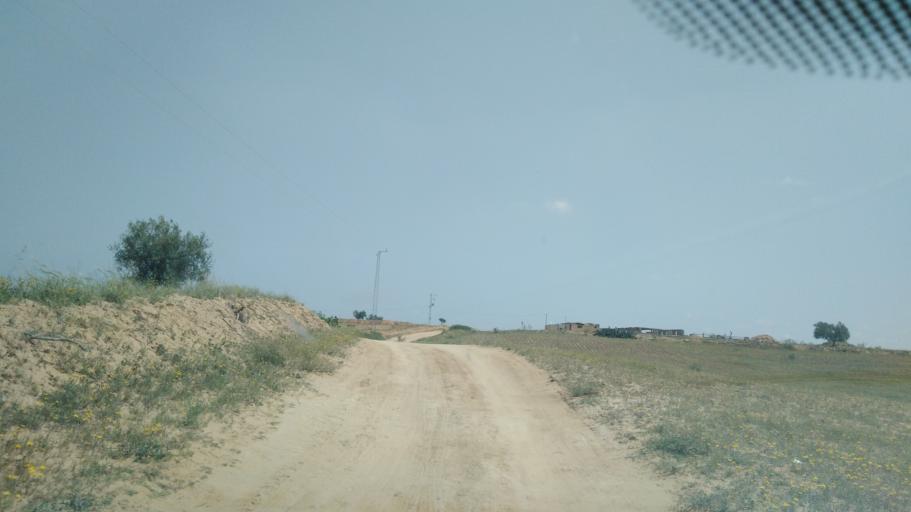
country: TN
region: Safaqis
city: Sfax
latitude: 34.7675
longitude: 10.5682
